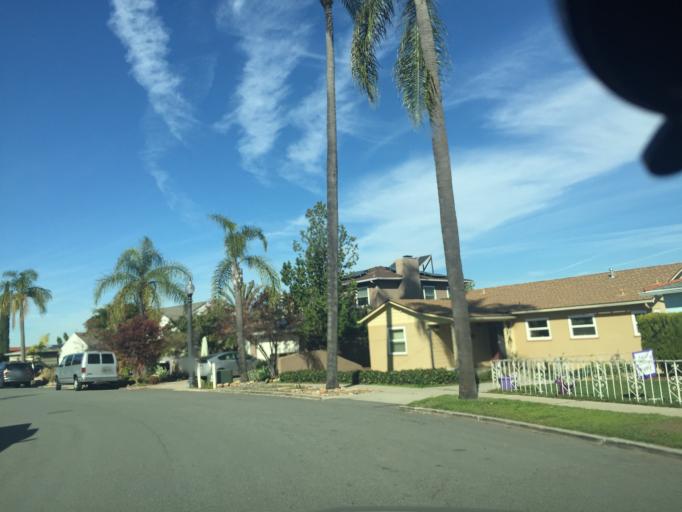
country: US
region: California
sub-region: San Diego County
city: Lemon Grove
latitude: 32.7673
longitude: -117.0890
